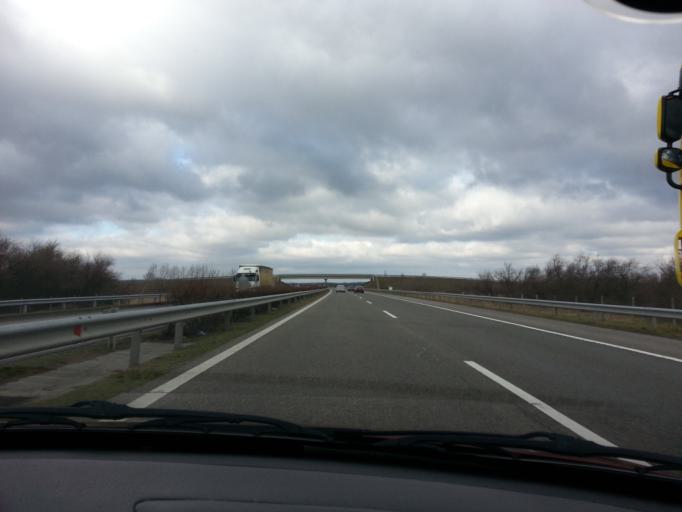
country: HU
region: Csongrad
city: Csengele
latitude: 46.5660
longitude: 19.8789
